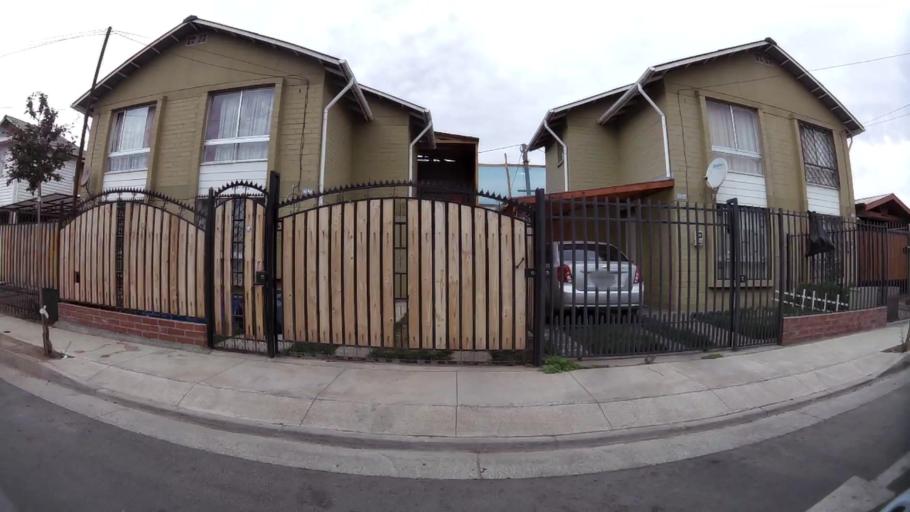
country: CL
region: O'Higgins
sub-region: Provincia de Cachapoal
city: Rancagua
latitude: -34.1309
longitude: -70.7325
